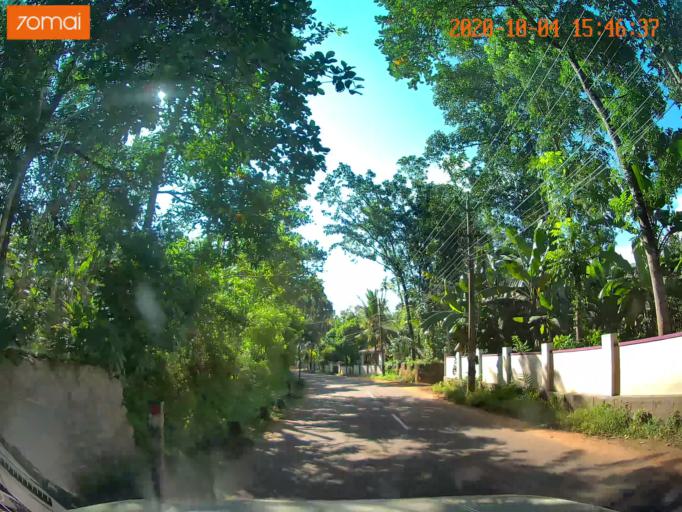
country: IN
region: Kerala
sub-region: Kottayam
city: Palackattumala
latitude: 9.7606
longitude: 76.5737
